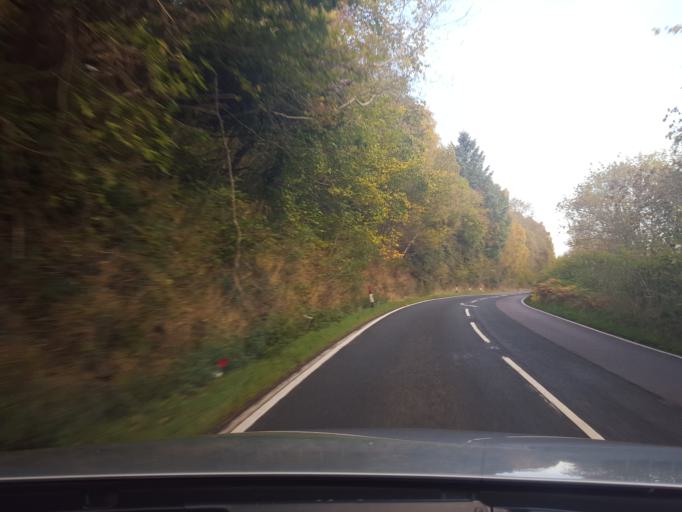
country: GB
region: Scotland
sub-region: Highland
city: Beauly
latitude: 57.3114
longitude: -4.4591
